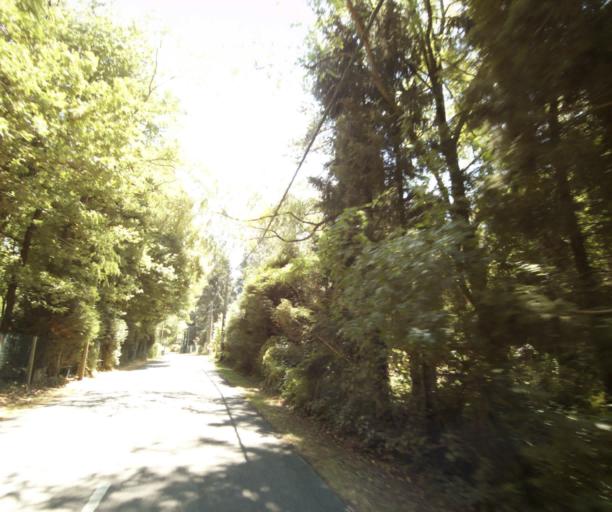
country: FR
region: Centre
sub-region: Departement du Loiret
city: Malesherbes
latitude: 48.2956
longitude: 2.4268
